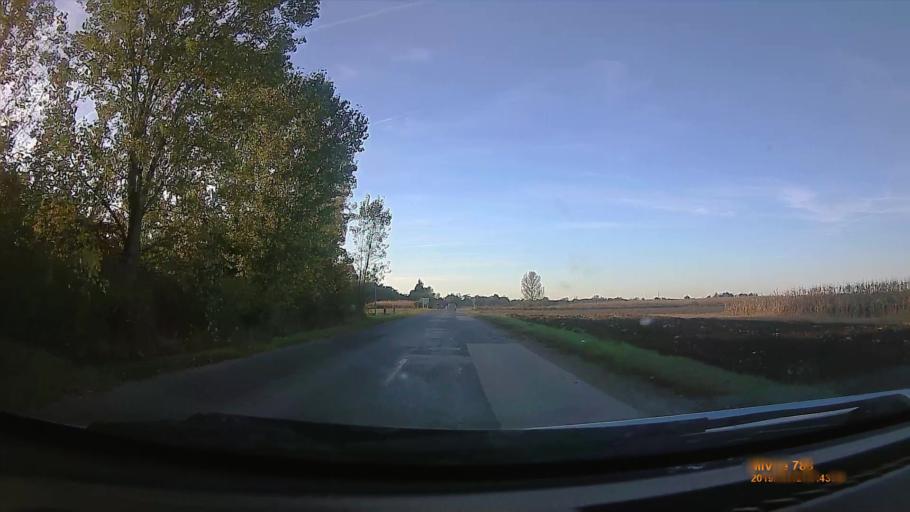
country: RO
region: Bihor
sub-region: Comuna Bors
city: Bors
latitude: 47.1970
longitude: 21.7884
